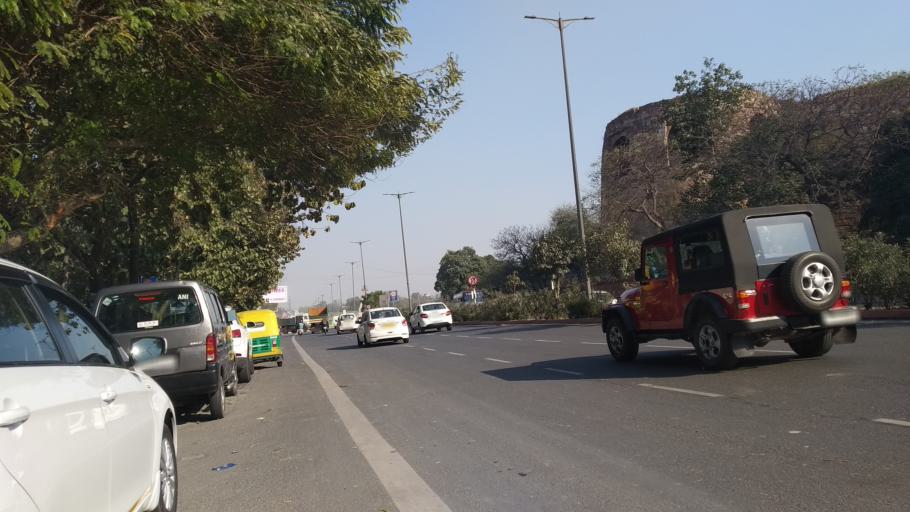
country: IN
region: NCT
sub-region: New Delhi
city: New Delhi
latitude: 28.6128
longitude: 77.2417
